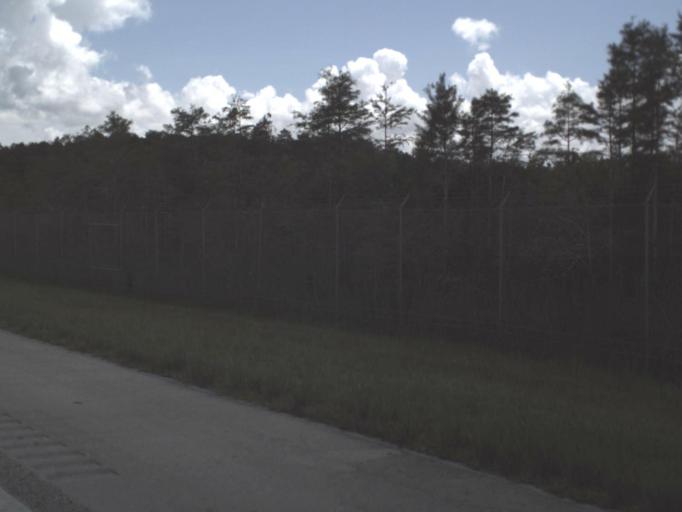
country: US
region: Florida
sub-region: Collier County
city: Immokalee
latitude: 26.1679
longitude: -81.1113
